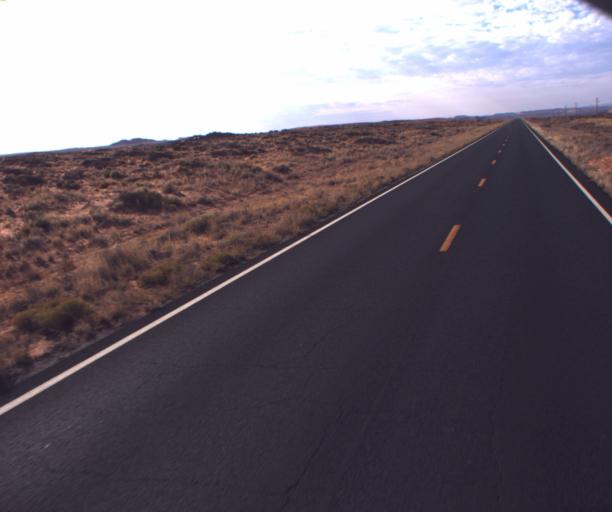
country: US
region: Arizona
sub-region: Apache County
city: Many Farms
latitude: 36.8343
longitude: -109.6431
